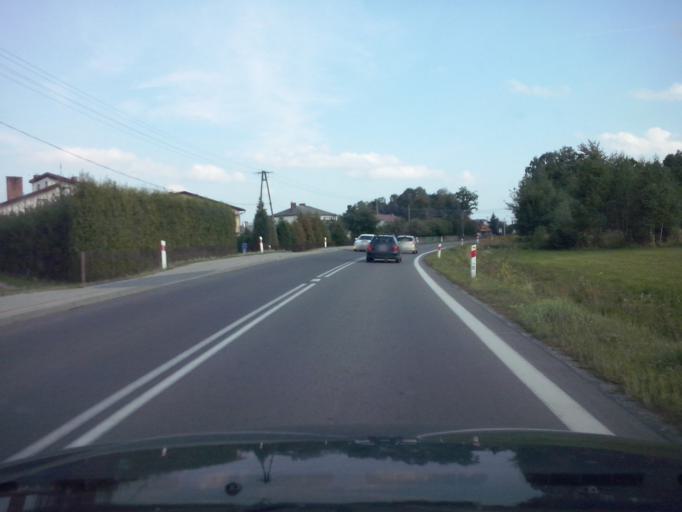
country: PL
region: Subcarpathian Voivodeship
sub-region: Powiat kolbuszowski
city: Cmolas
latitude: 50.2596
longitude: 21.7317
